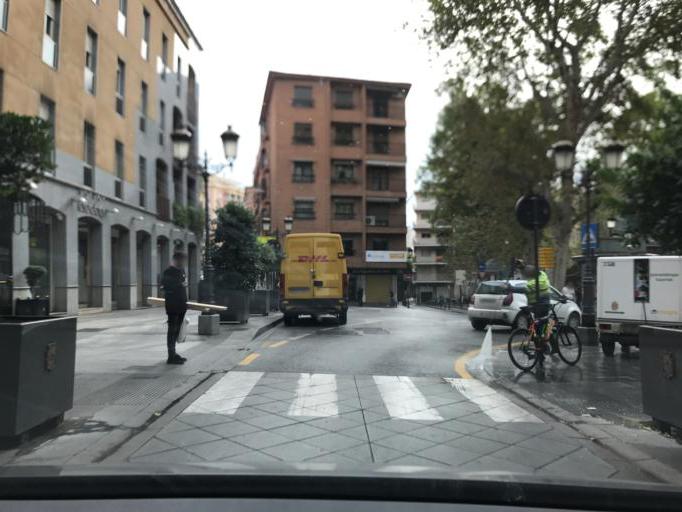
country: ES
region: Andalusia
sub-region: Provincia de Granada
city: Granada
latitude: 37.1728
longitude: -3.5977
